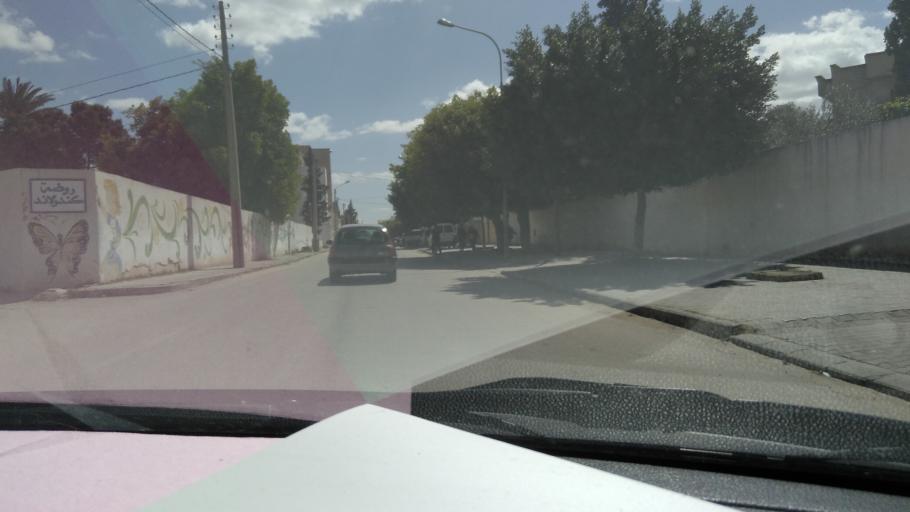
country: TN
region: Al Qayrawan
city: Kairouan
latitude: 35.6717
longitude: 10.1049
